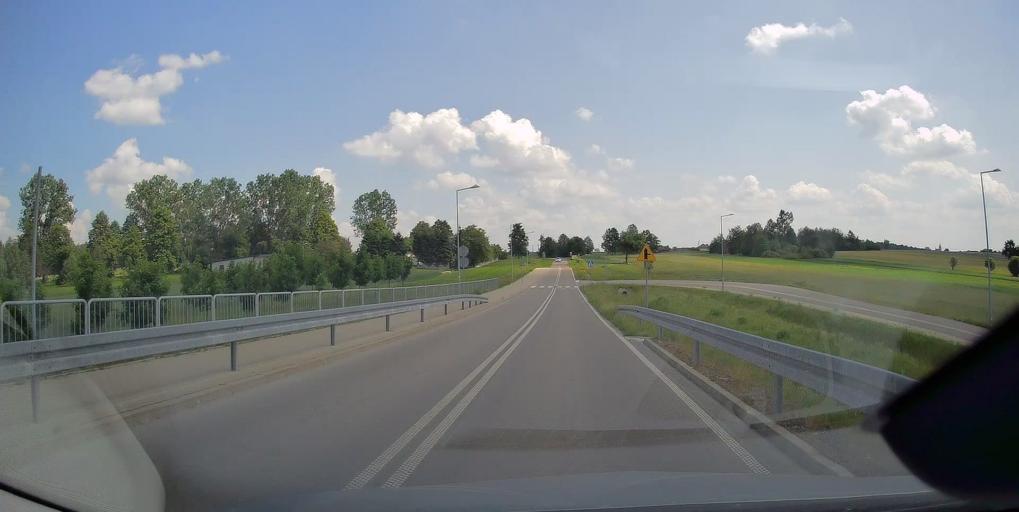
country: PL
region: Lodz Voivodeship
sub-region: Powiat tomaszowski
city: Czerniewice
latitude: 51.6934
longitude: 20.2135
